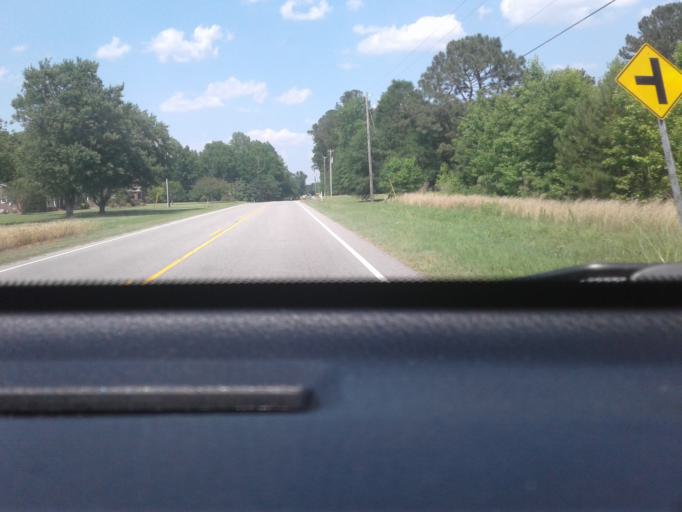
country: US
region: North Carolina
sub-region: Cumberland County
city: Eastover
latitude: 35.1325
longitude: -78.7516
